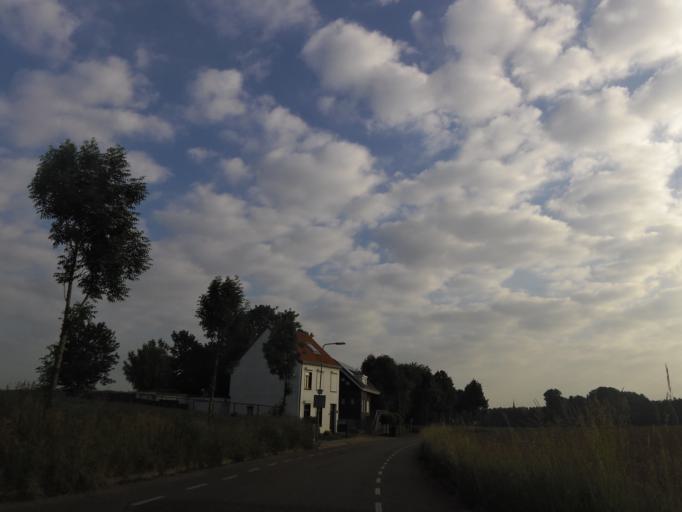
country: NL
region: Limburg
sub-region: Gemeente Onderbanken
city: Merkelbeek
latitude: 50.9854
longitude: 5.9421
